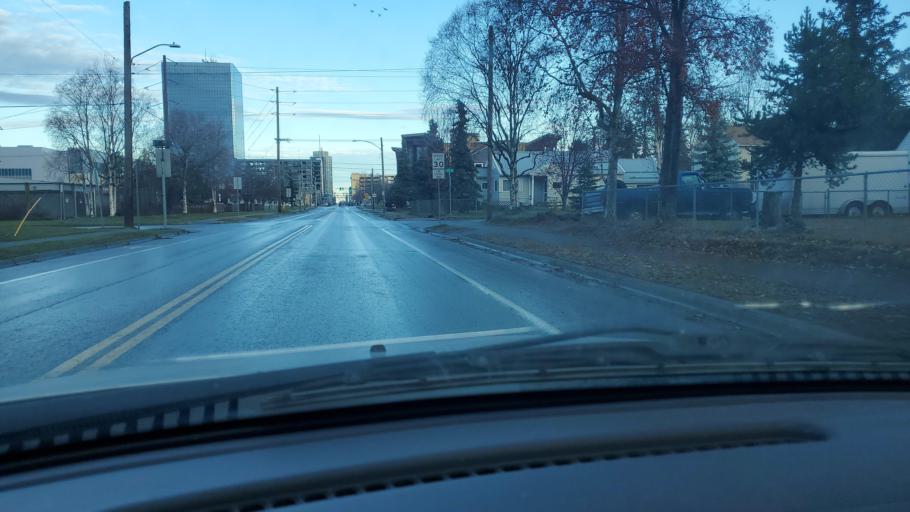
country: US
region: Alaska
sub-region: Anchorage Municipality
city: Anchorage
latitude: 61.2113
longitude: -149.8915
